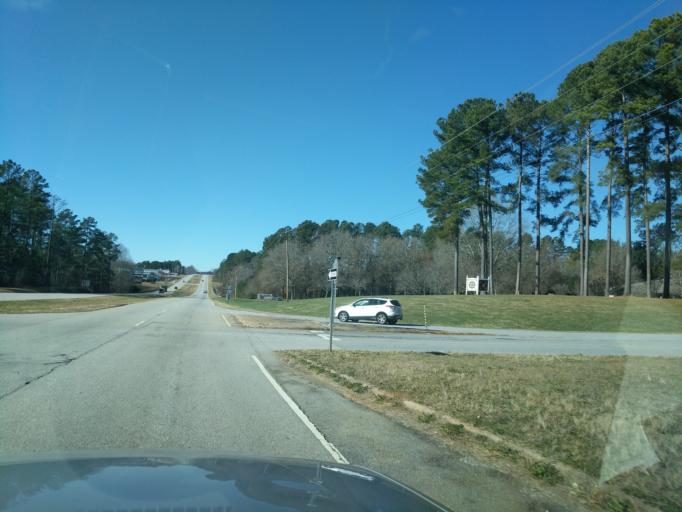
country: US
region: South Carolina
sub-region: Oconee County
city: Westminster
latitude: 34.6648
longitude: -83.0411
